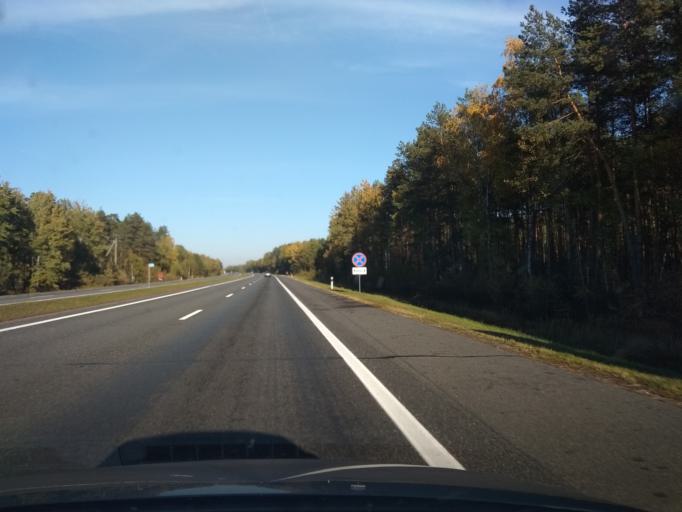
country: BY
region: Brest
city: Nyakhachava
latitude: 52.5790
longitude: 25.1202
